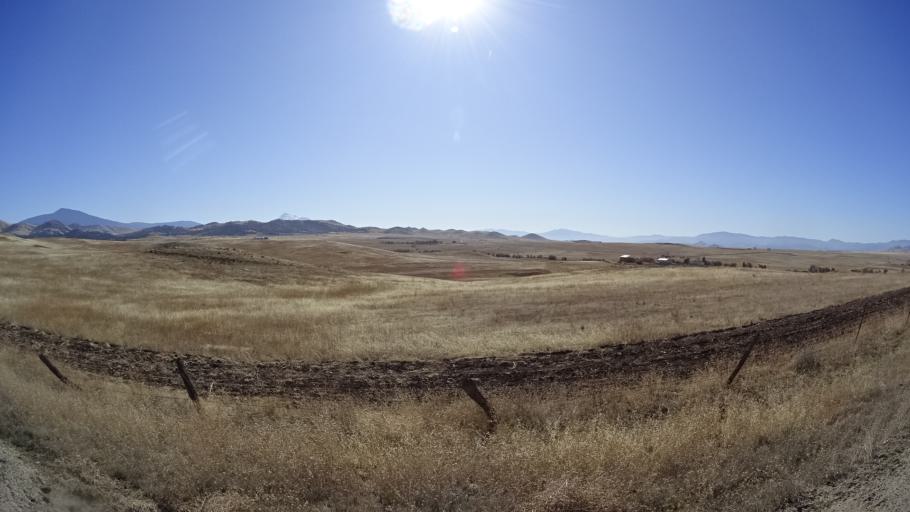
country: US
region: California
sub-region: Siskiyou County
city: Montague
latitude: 41.8298
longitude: -122.4151
